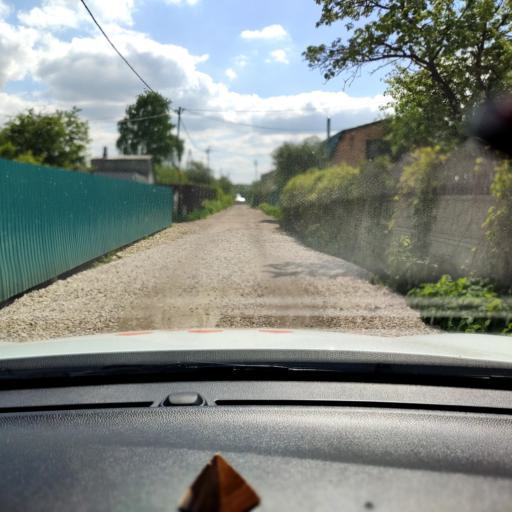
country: RU
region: Tatarstan
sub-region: Gorod Kazan'
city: Kazan
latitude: 55.8614
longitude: 49.1851
